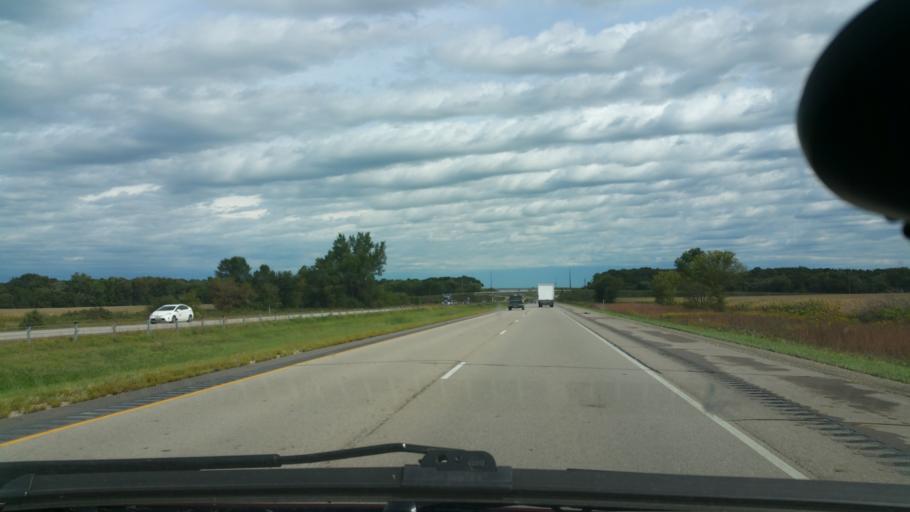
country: US
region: Minnesota
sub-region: Steele County
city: Owatonna
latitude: 44.0470
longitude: -93.2493
